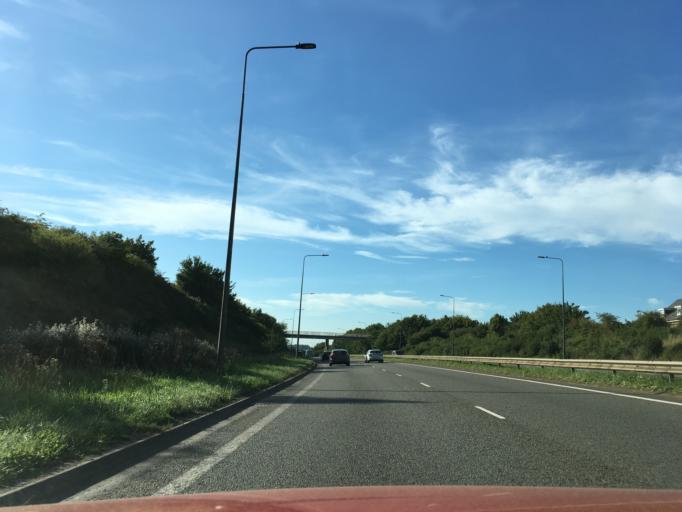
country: GB
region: England
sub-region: South Gloucestershire
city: Siston
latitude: 51.4938
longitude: -2.4720
